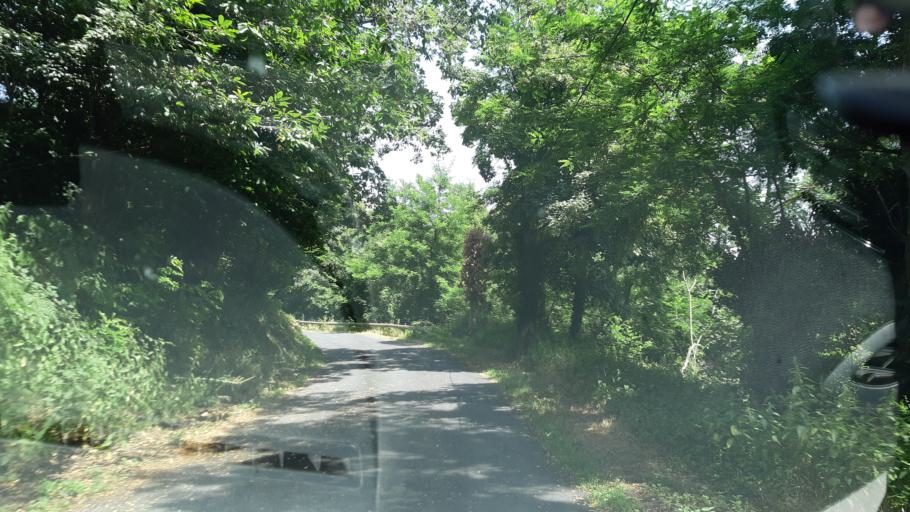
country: FR
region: Languedoc-Roussillon
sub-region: Departement des Pyrenees-Orientales
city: Arles
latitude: 42.5449
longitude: 2.5873
